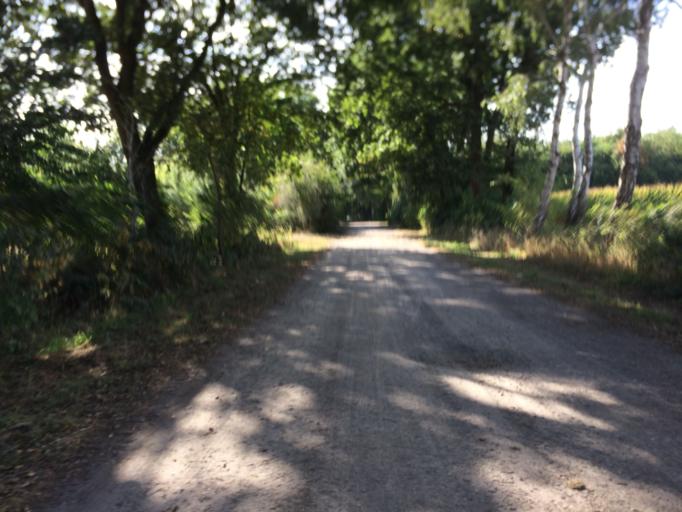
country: DE
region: North Rhine-Westphalia
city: Dorsten
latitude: 51.6945
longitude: 7.0252
